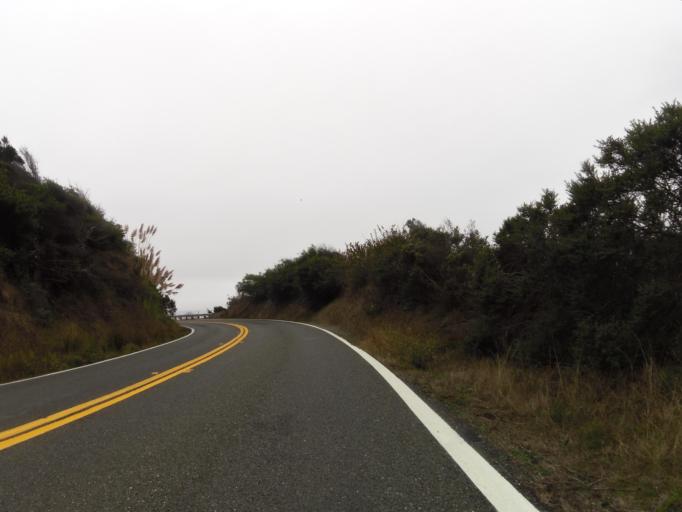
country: US
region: California
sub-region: Sonoma County
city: Monte Rio
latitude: 38.4573
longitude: -123.1365
